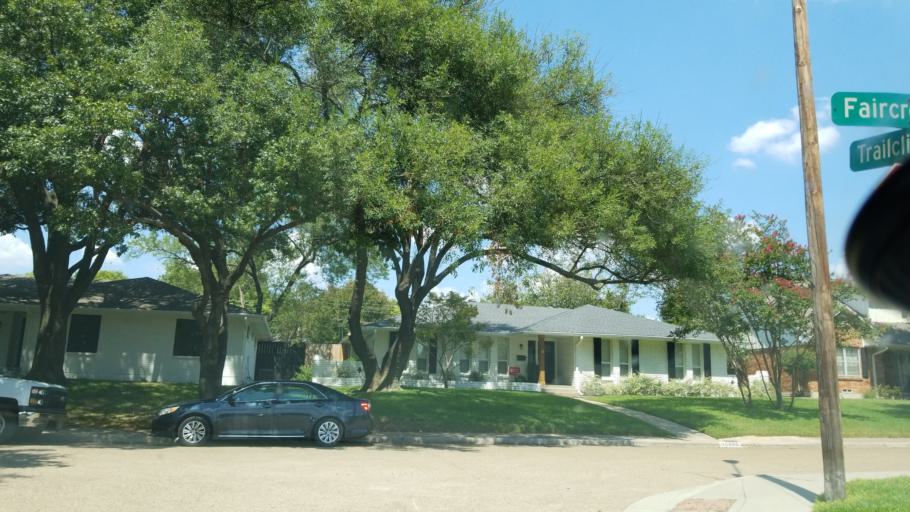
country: US
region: Texas
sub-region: Dallas County
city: Richardson
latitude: 32.8895
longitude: -96.7139
